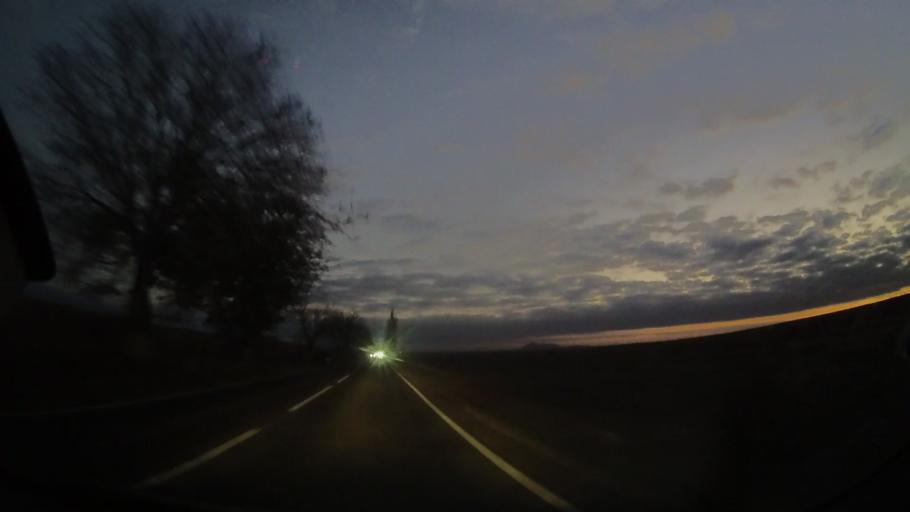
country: RO
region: Tulcea
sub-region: Comuna Frecatei
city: Cataloi
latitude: 45.0895
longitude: 28.7410
